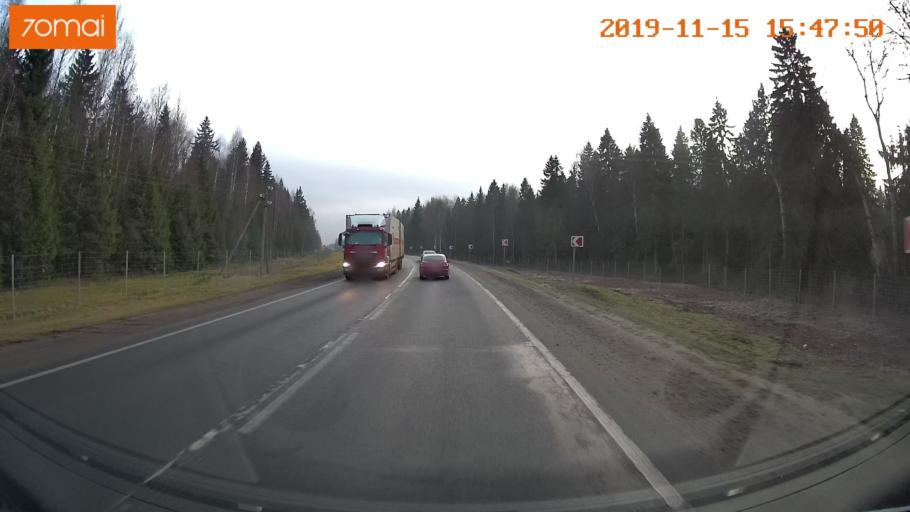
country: RU
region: Jaroslavl
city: Danilov
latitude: 57.9341
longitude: 40.0067
